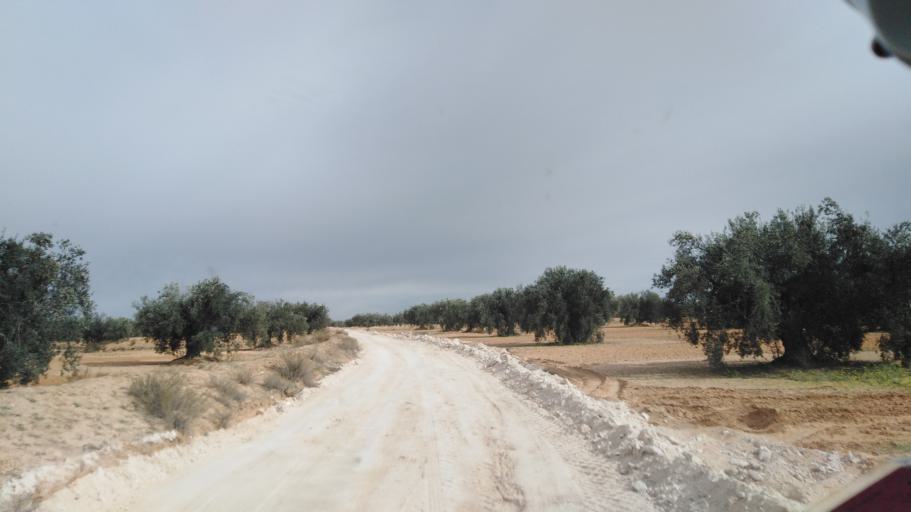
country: TN
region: Safaqis
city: Bi'r `Ali Bin Khalifah
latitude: 34.8109
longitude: 10.3054
